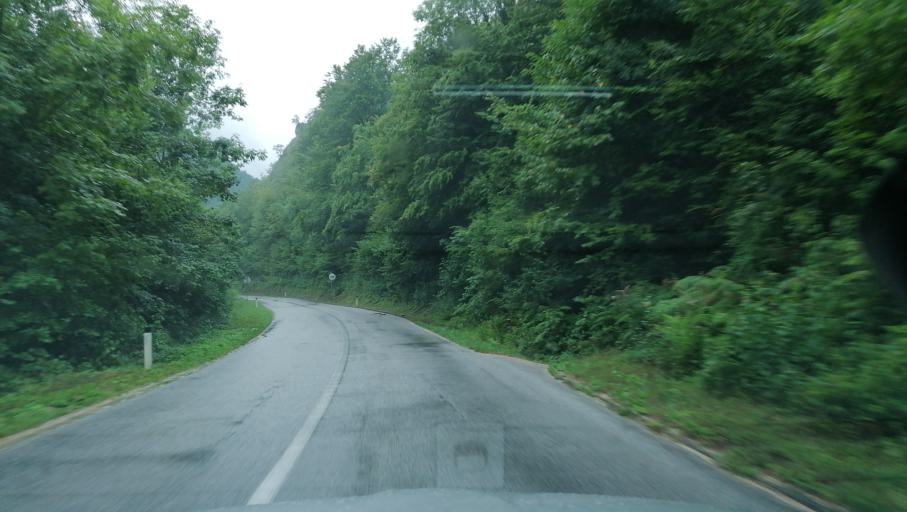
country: BA
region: Republika Srpska
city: Foca
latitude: 43.3313
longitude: 18.6884
